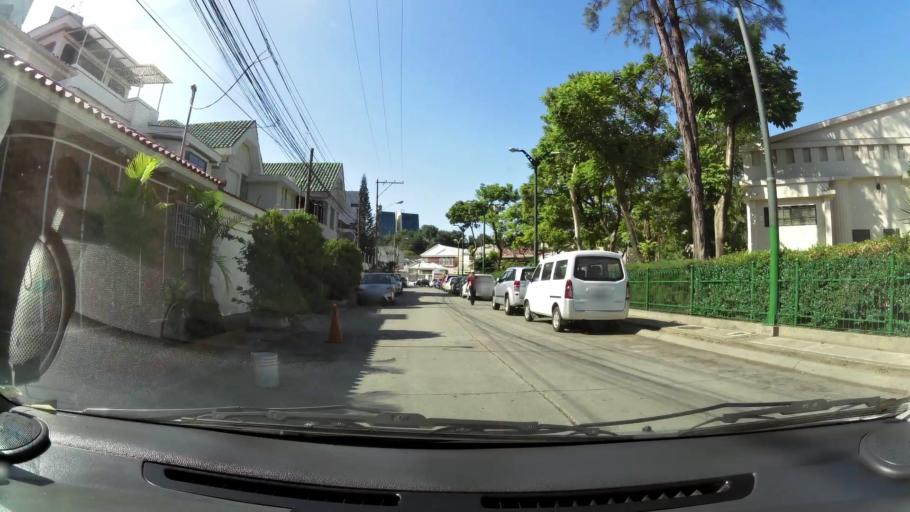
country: EC
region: Guayas
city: Guayaquil
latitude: -2.1638
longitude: -79.8989
